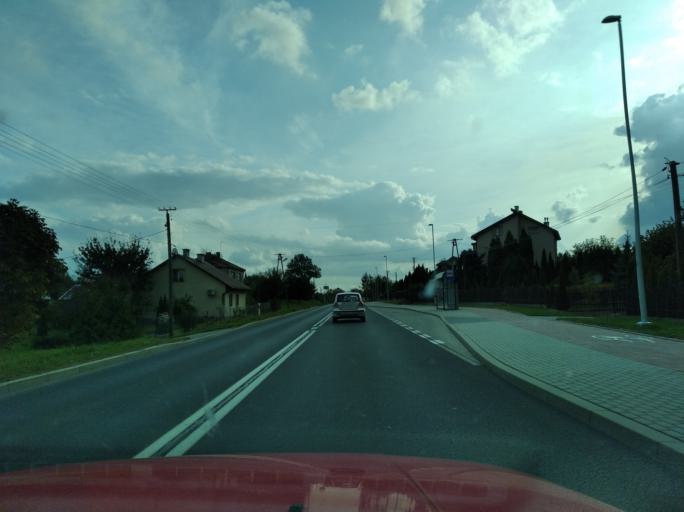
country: PL
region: Subcarpathian Voivodeship
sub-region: Powiat jaroslawski
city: Pawlosiow
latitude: 49.9938
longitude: 22.6652
